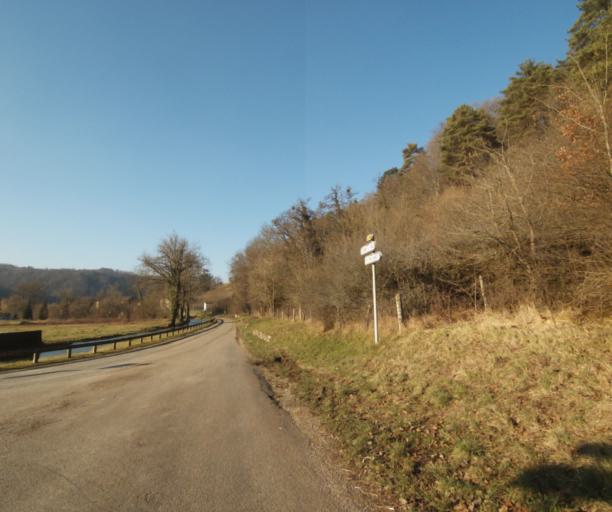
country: FR
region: Champagne-Ardenne
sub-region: Departement de la Haute-Marne
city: Joinville
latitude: 48.4911
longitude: 5.1985
